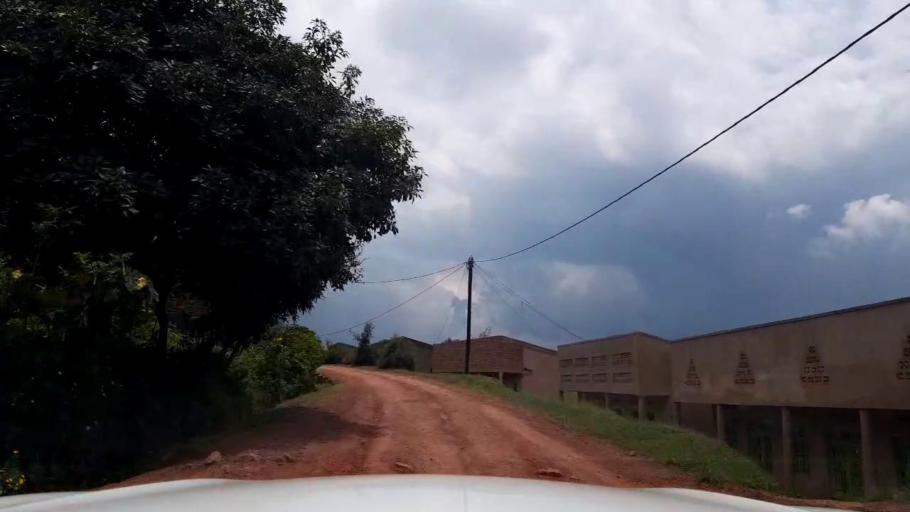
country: RW
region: Northern Province
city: Byumba
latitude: -1.4984
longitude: 29.9346
